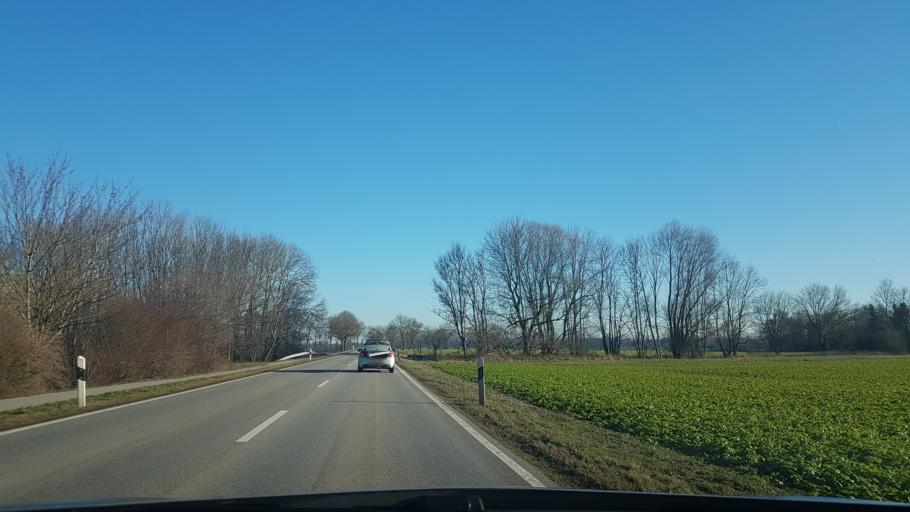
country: DE
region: Bavaria
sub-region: Upper Bavaria
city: Oberding
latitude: 48.3093
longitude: 11.8159
